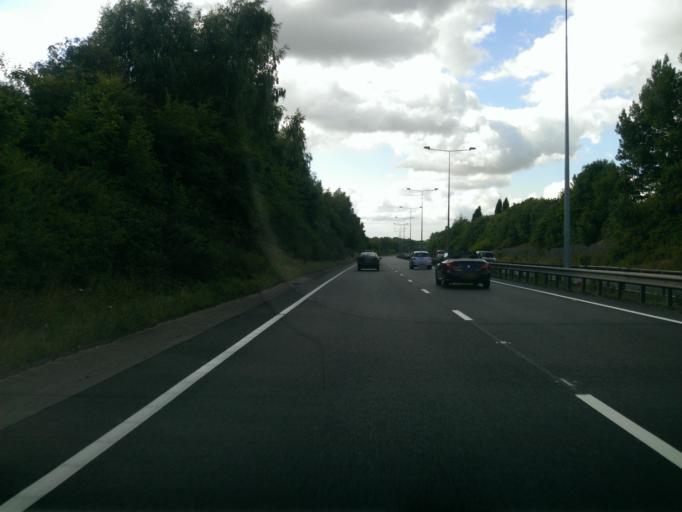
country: GB
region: England
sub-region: Staffordshire
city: Fazeley
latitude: 52.6079
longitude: -1.6532
